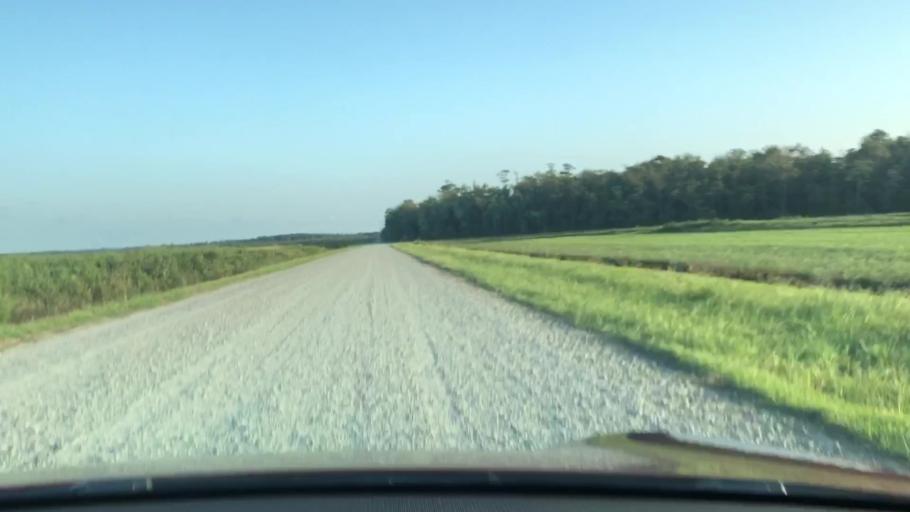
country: US
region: North Carolina
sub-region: Dare County
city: Manteo
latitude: 35.8467
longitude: -75.8609
